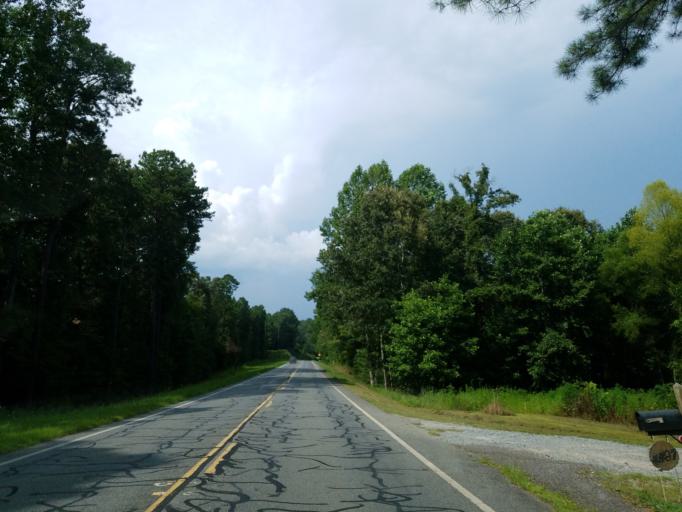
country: US
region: Georgia
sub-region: Gilmer County
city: Ellijay
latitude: 34.6349
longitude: -84.5782
